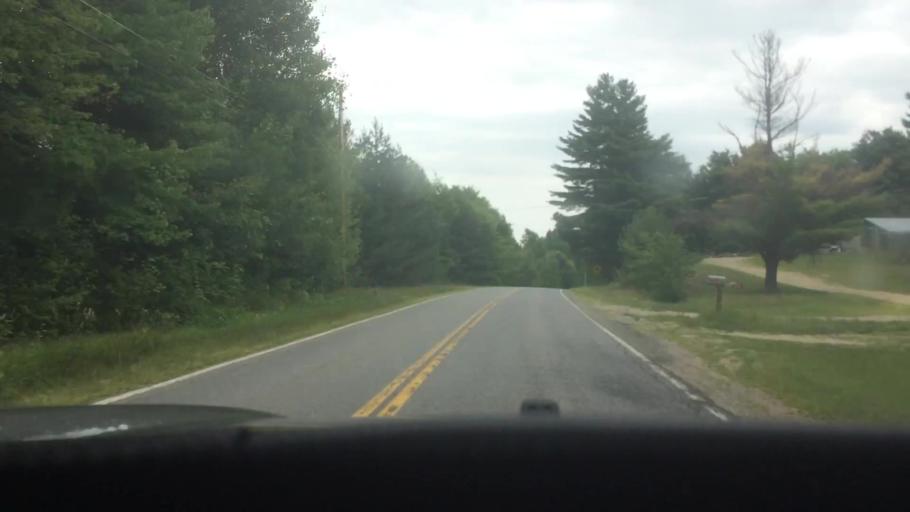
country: US
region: New York
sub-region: St. Lawrence County
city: Hannawa Falls
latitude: 44.6173
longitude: -74.8638
